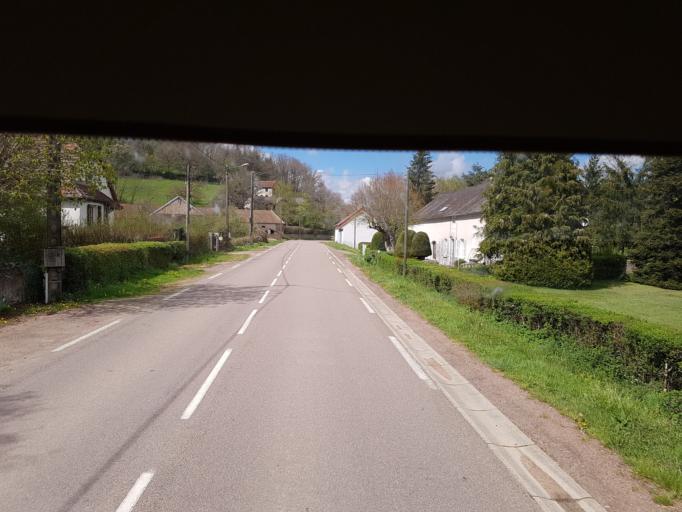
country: FR
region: Bourgogne
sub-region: Departement de Saone-et-Loire
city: Autun
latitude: 47.1013
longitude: 4.2308
